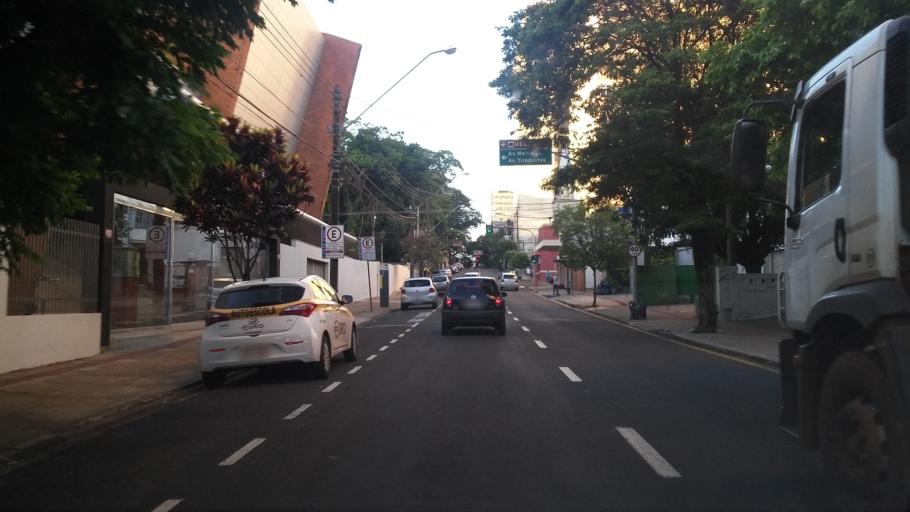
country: BR
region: Parana
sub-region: Londrina
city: Londrina
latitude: -23.3153
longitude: -51.1589
